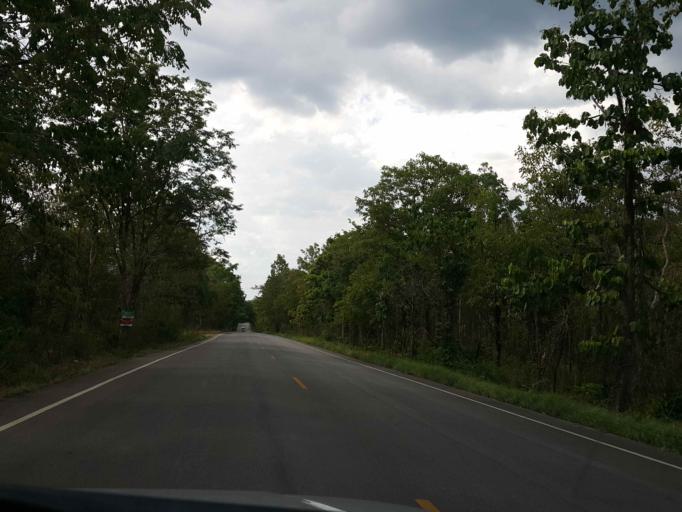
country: TH
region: Sukhothai
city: Thung Saliam
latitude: 17.3811
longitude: 99.4000
